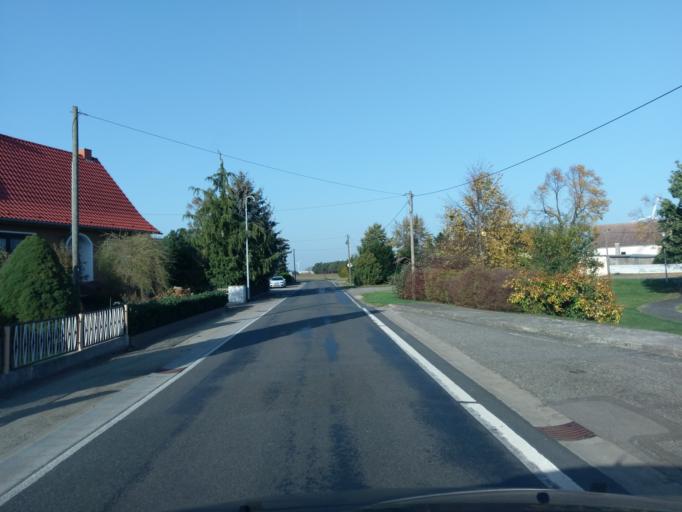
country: DE
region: Brandenburg
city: Falkenberg
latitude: 51.5184
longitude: 13.2985
